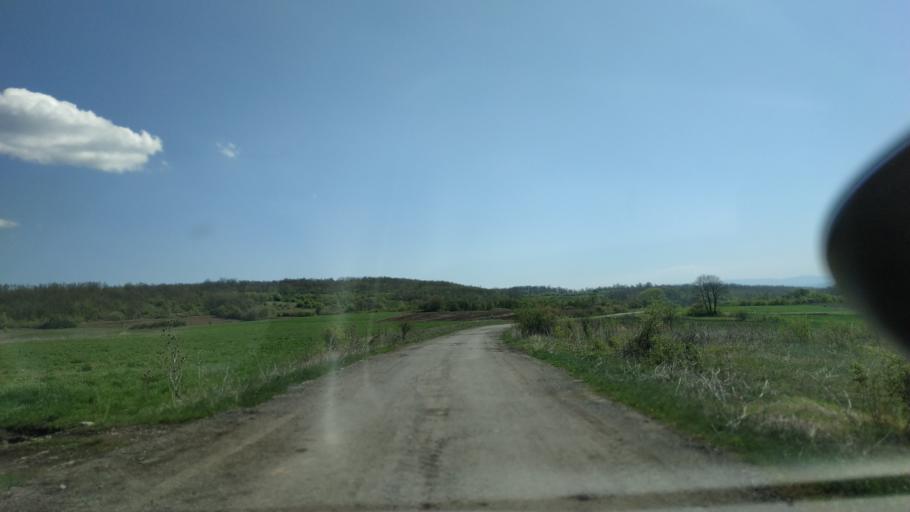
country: RS
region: Central Serbia
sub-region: Zajecarski Okrug
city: Soko Banja
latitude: 43.5150
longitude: 21.9055
